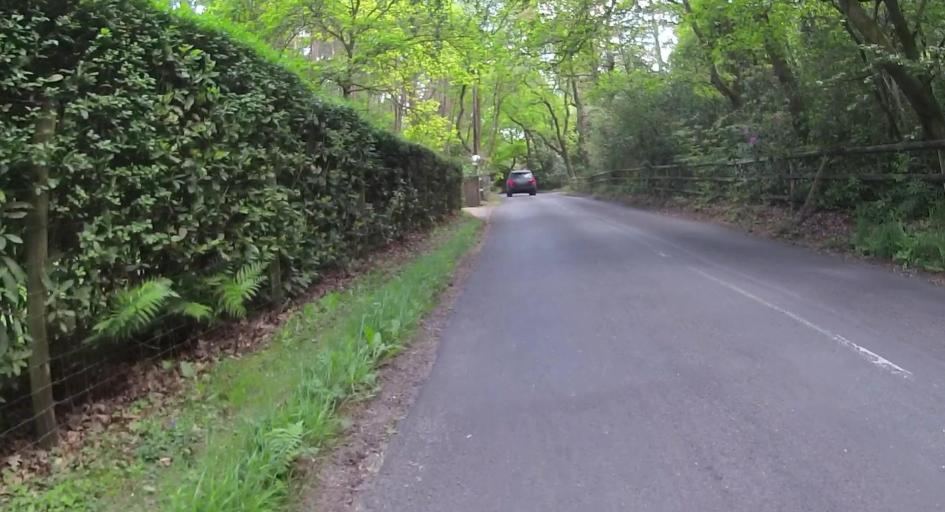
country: GB
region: England
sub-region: Surrey
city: Farnham
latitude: 51.1897
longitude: -0.7846
